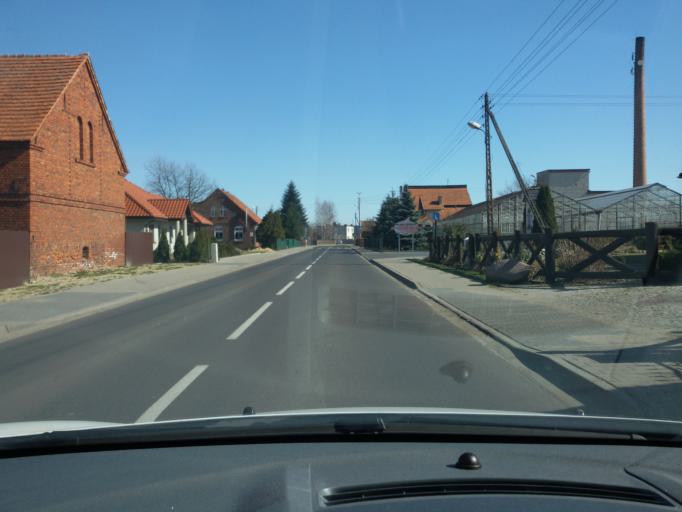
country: PL
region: Greater Poland Voivodeship
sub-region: Powiat leszczynski
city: Rydzyna
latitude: 51.7715
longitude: 16.7212
